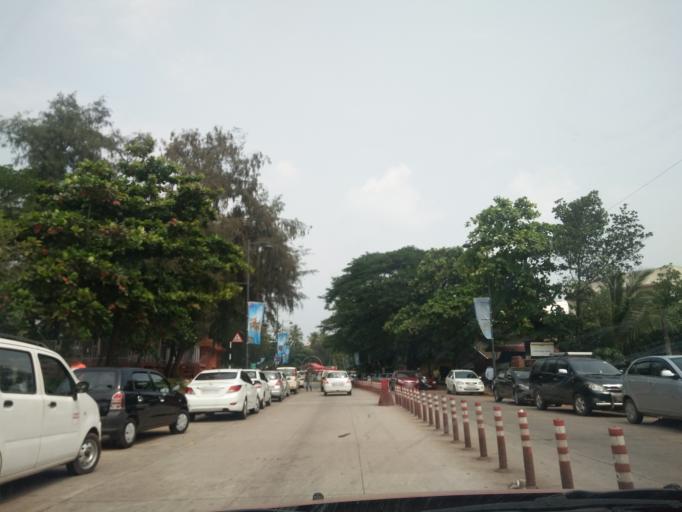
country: IN
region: Goa
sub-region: North Goa
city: Panaji
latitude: 15.4817
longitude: 73.8088
